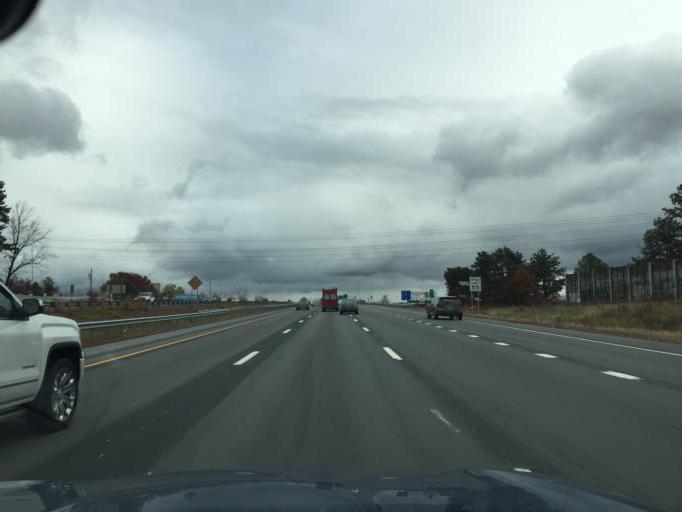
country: US
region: New Hampshire
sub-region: Hillsborough County
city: Manchester
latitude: 42.9529
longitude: -71.4475
